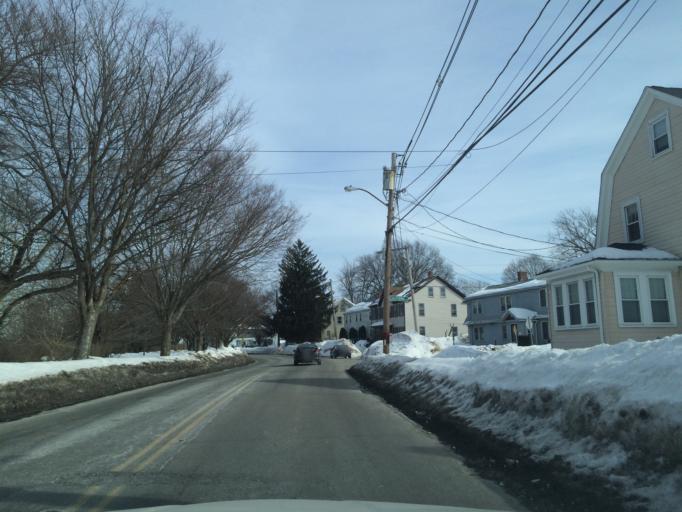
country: US
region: Massachusetts
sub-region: Middlesex County
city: Watertown
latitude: 42.3645
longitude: -71.1929
